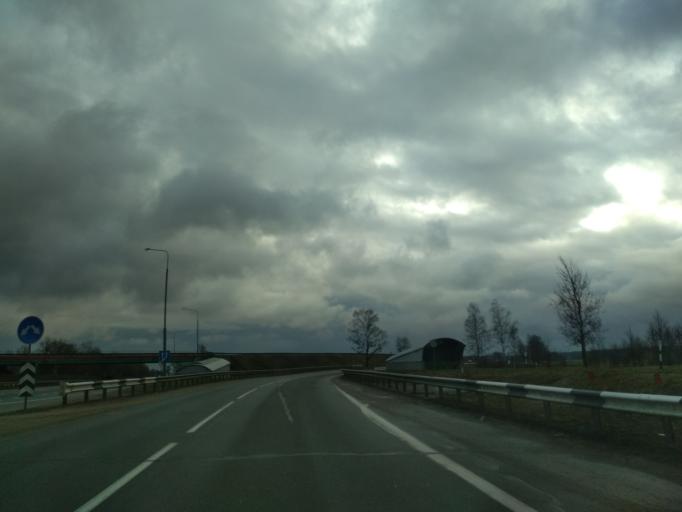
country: BY
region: Minsk
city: Pryvol'ny
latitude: 53.7931
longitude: 27.8172
